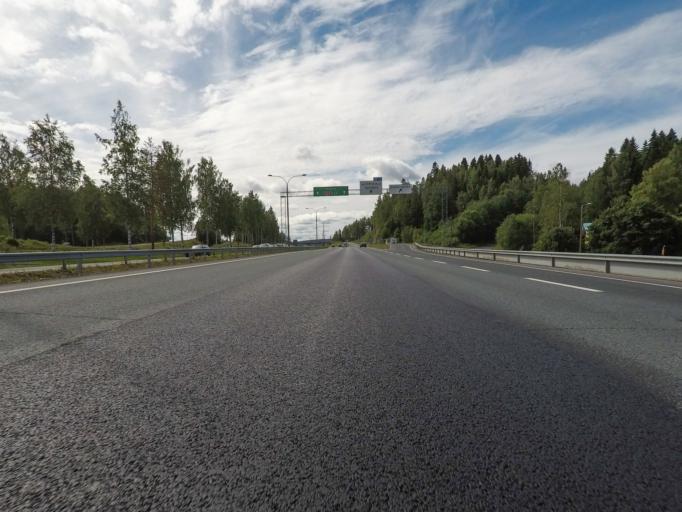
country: FI
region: Northern Savo
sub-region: Kuopio
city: Kuopio
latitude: 62.9621
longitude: 27.6940
